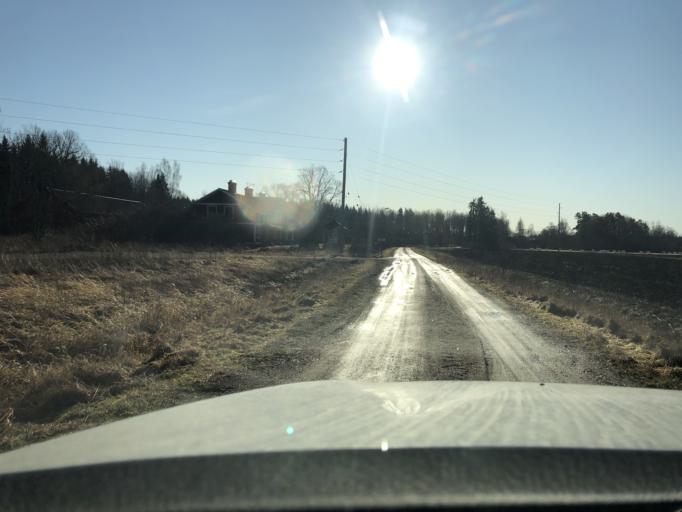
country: SE
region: Gaevleborg
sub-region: Gavle Kommun
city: Hedesunda
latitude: 60.2966
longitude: 16.8870
